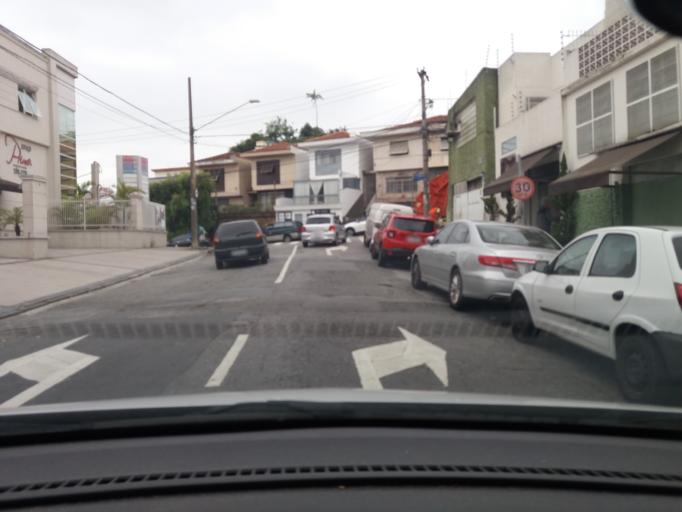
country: BR
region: Sao Paulo
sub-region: Sao Paulo
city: Sao Paulo
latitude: -23.4823
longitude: -46.6213
